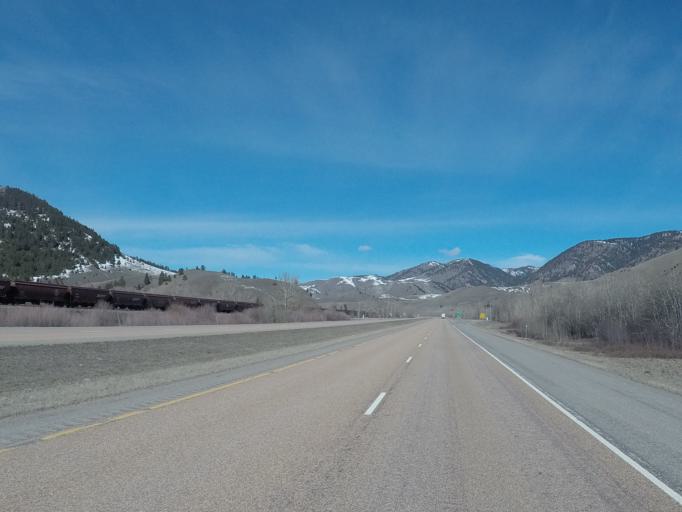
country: US
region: Montana
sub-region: Granite County
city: Philipsburg
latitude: 46.6885
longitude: -113.1983
